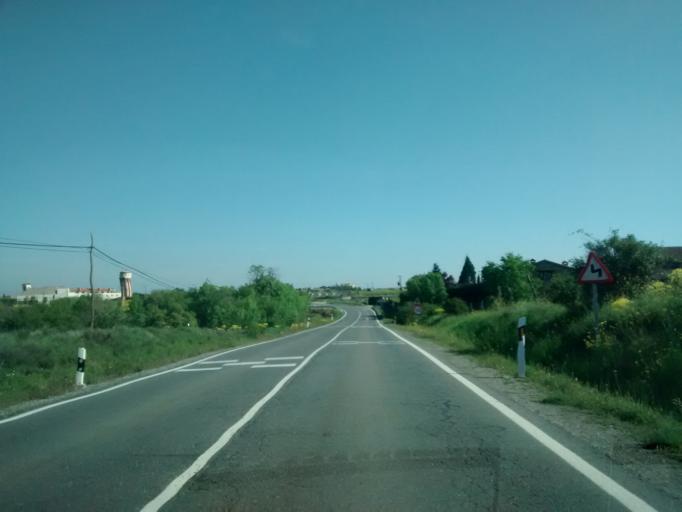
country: ES
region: Castille and Leon
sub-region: Provincia de Segovia
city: Trescasas
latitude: 40.9521
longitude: -4.0339
